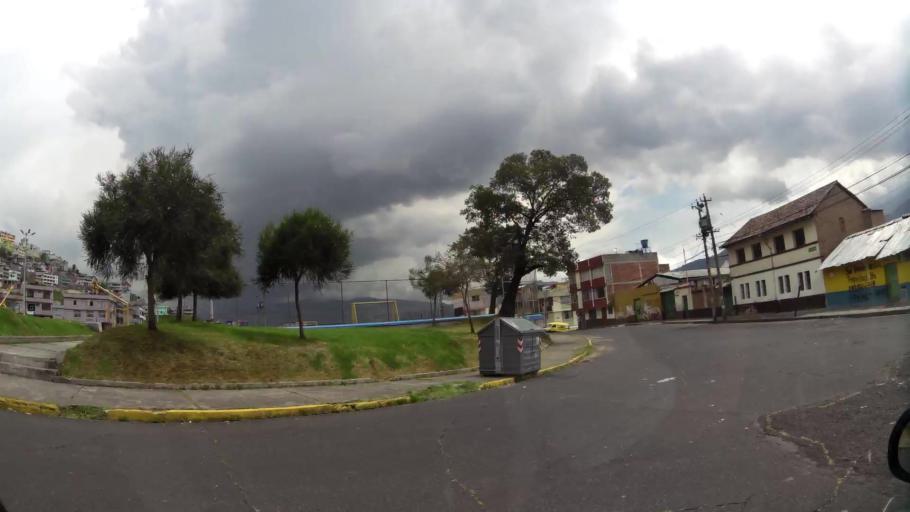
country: EC
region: Pichincha
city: Quito
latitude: -0.2572
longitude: -78.5160
